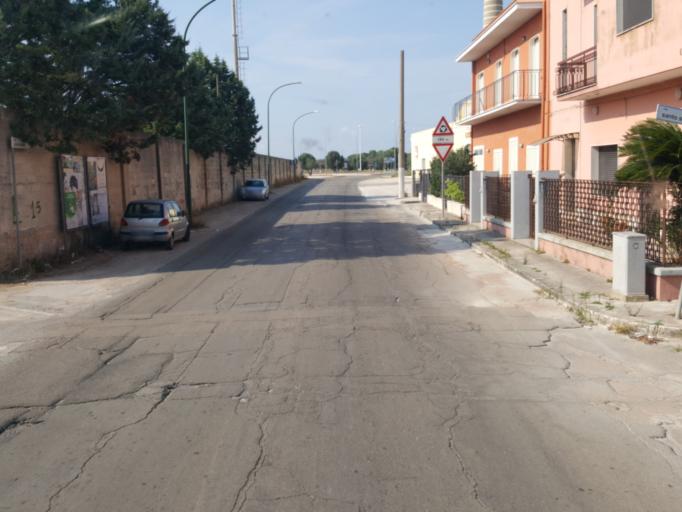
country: IT
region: Apulia
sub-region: Provincia di Lecce
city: Campi Salentina
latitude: 40.4045
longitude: 18.0212
